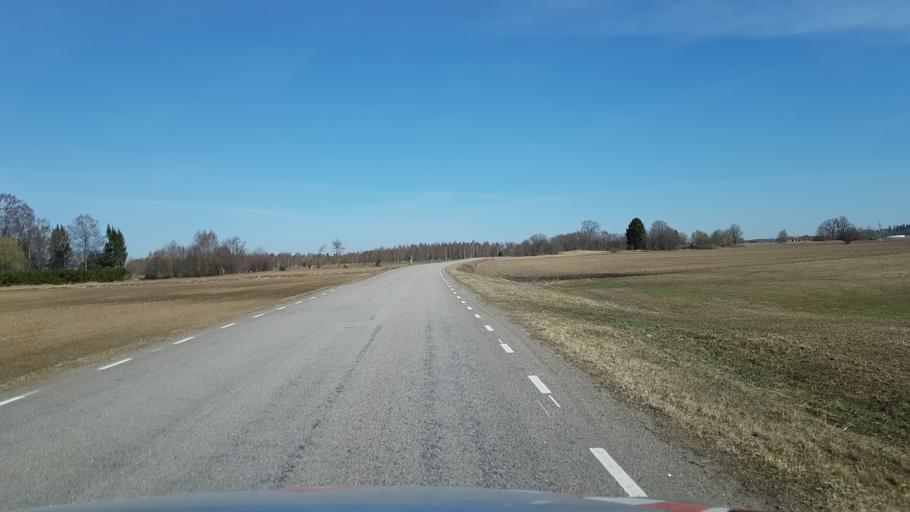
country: EE
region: Laeaene-Virumaa
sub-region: Vaeike-Maarja vald
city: Vaike-Maarja
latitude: 59.2165
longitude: 26.3347
